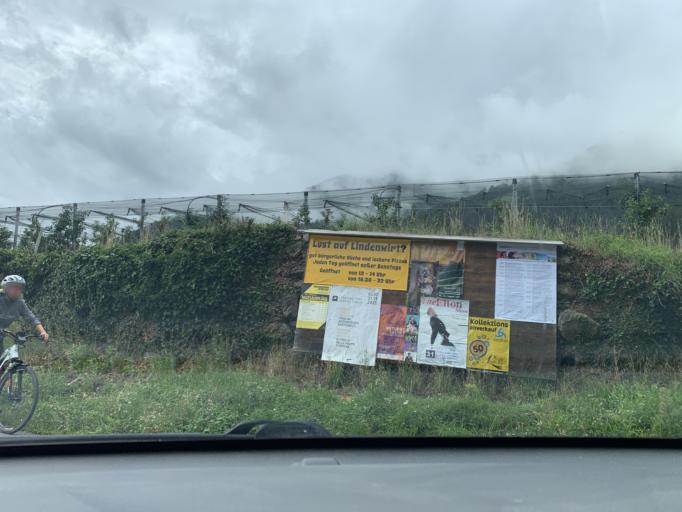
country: IT
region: Trentino-Alto Adige
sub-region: Bolzano
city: Tirolo
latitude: 46.6978
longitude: 11.1524
